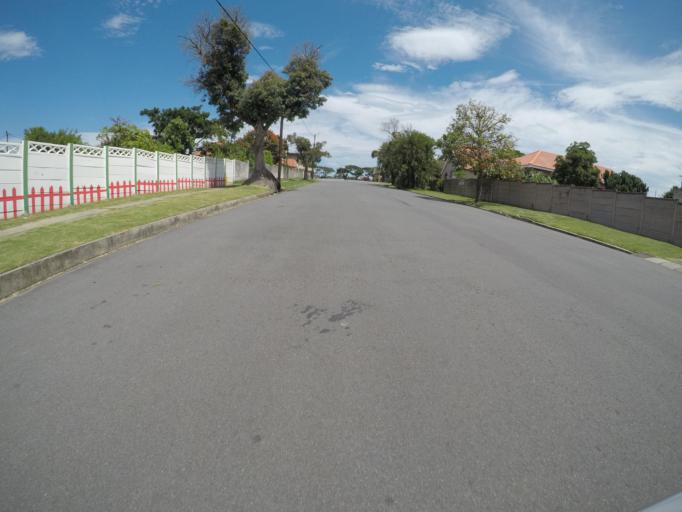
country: ZA
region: Eastern Cape
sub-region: Buffalo City Metropolitan Municipality
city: East London
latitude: -33.0335
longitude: 27.8597
